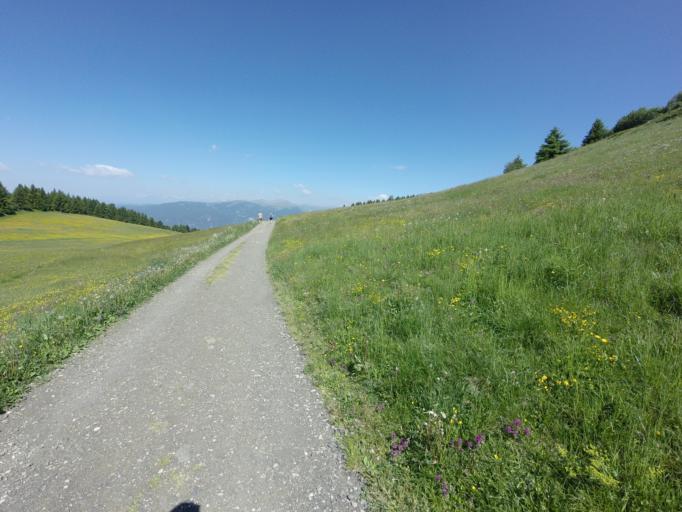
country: IT
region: Trentino-Alto Adige
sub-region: Bolzano
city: Castelrotto
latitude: 46.5519
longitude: 11.6021
